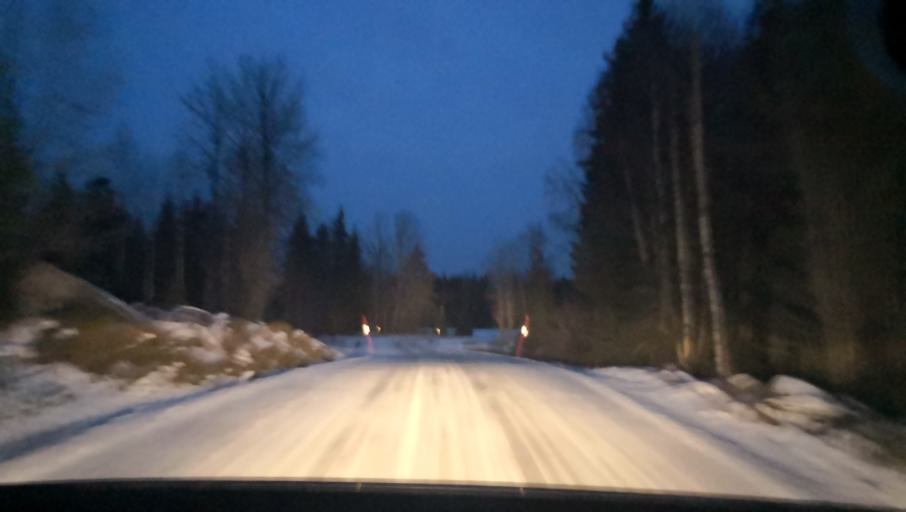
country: SE
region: Uppsala
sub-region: Heby Kommun
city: Tarnsjo
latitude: 60.2454
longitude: 16.7232
